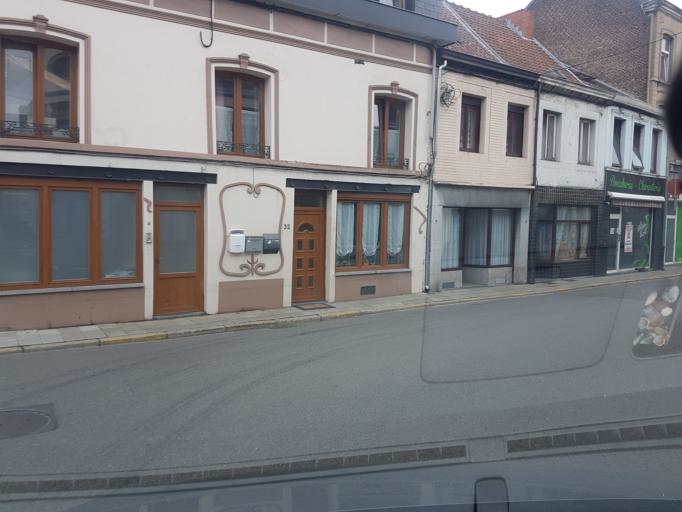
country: BE
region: Wallonia
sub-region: Province de Namur
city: Andenne
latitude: 50.4858
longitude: 5.0968
